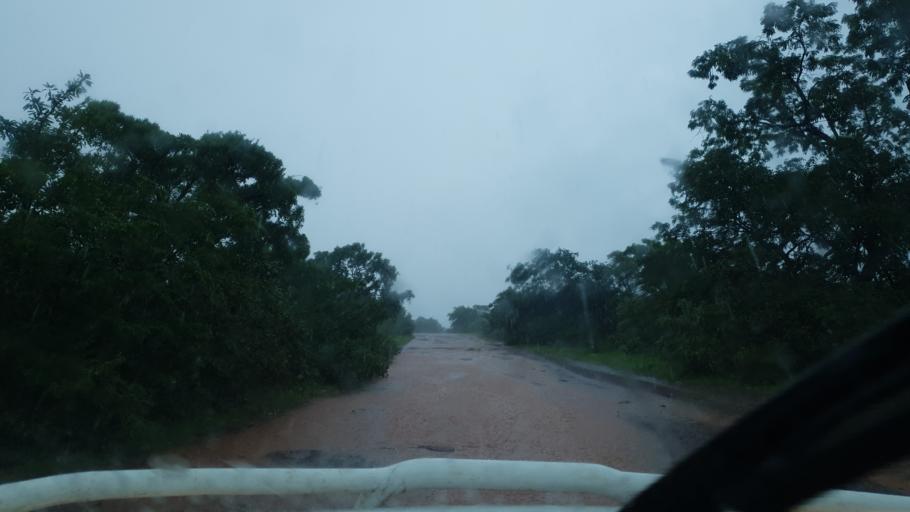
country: ML
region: Sikasso
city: Kolondieba
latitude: 11.6195
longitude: -6.6796
